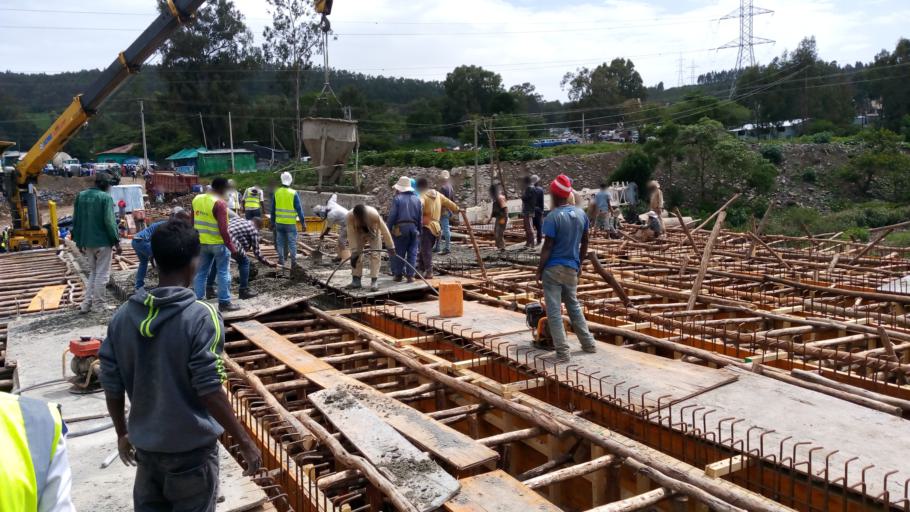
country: ET
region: Amhara
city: Gondar
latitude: 12.5521
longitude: 37.4251
